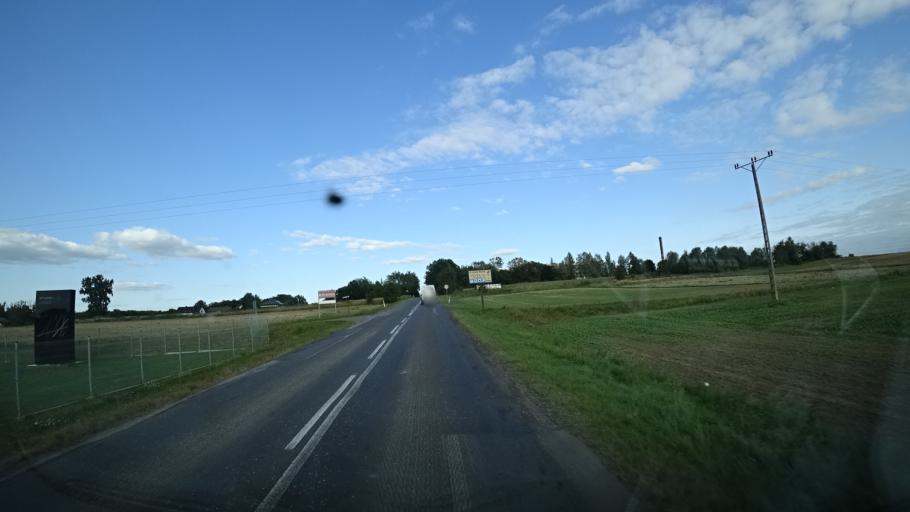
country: PL
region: Silesian Voivodeship
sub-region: Powiat gliwicki
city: Sosnicowice
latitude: 50.2753
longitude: 18.4610
